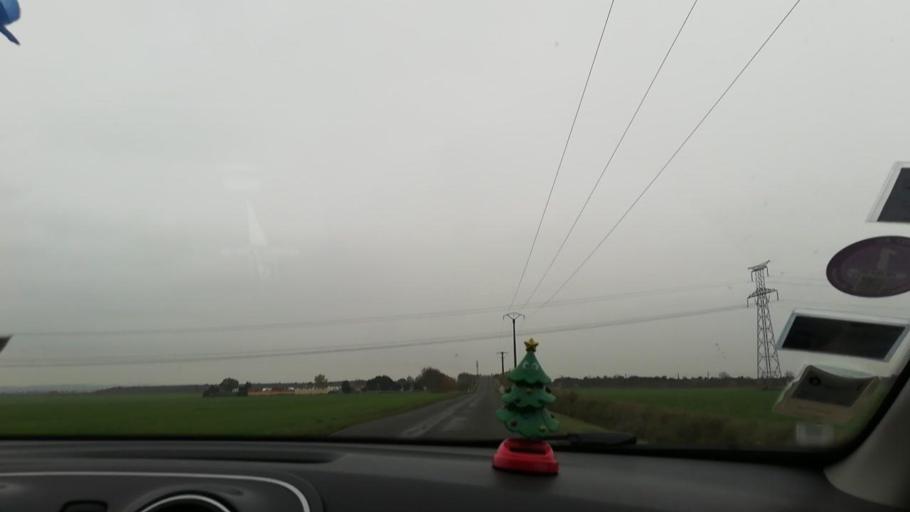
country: FR
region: Ile-de-France
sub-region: Departement de Seine-et-Marne
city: Charny
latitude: 48.9687
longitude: 2.7393
